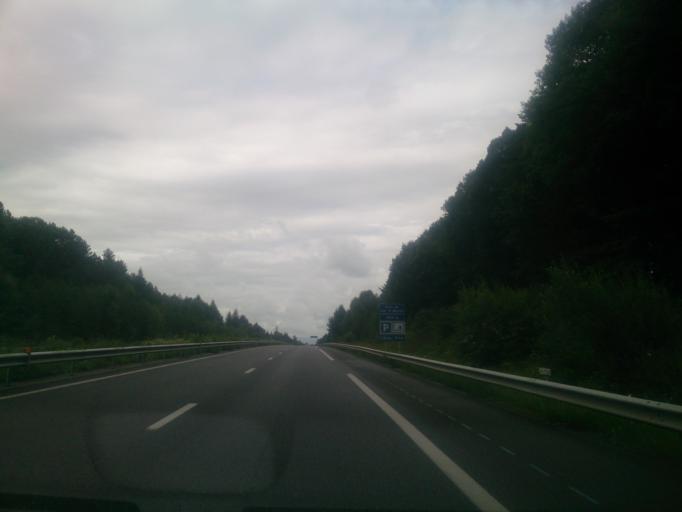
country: FR
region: Midi-Pyrenees
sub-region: Departement des Hautes-Pyrenees
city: La Barthe-de-Neste
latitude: 43.0999
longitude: 0.3646
